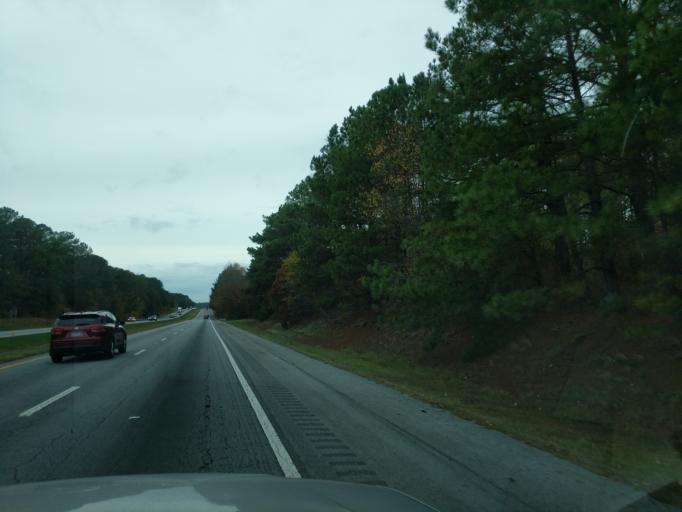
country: US
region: South Carolina
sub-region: Laurens County
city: Joanna
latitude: 34.4285
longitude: -81.7301
